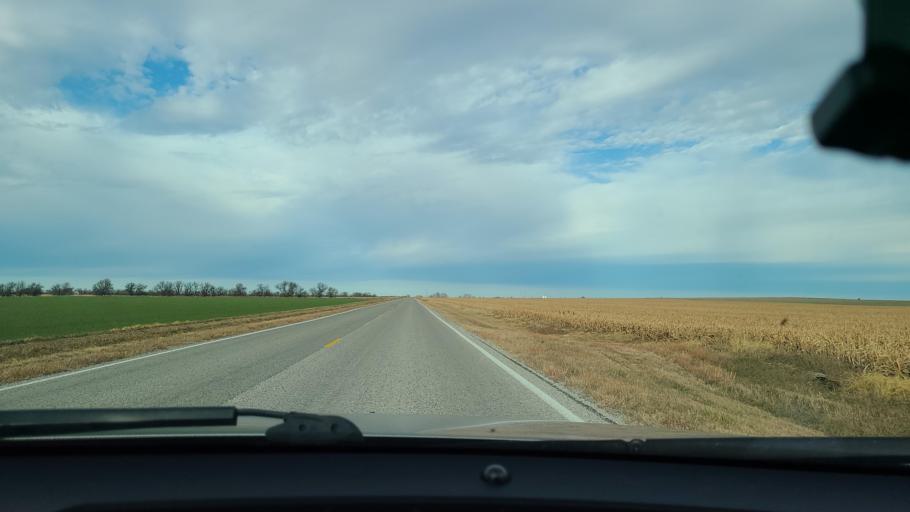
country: US
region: Kansas
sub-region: McPherson County
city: Inman
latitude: 38.3223
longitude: -97.9246
